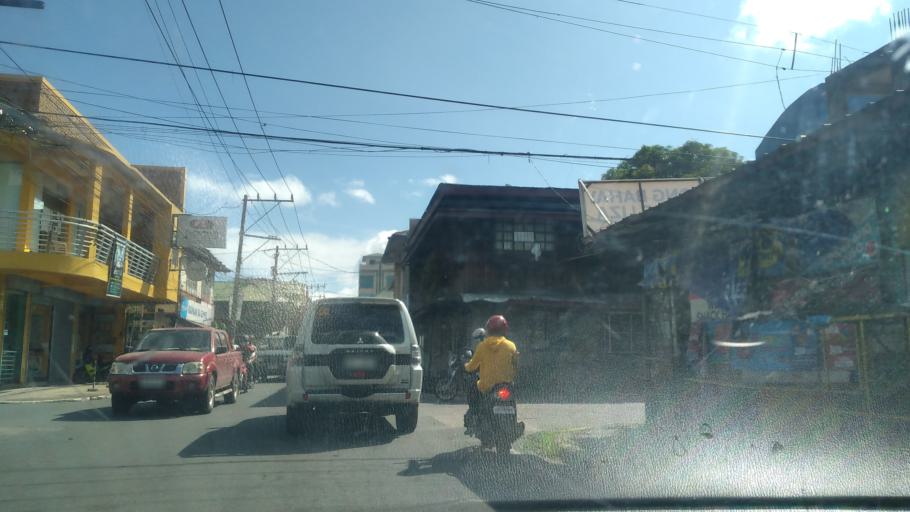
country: PH
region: Calabarzon
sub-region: Province of Quezon
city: Lucena
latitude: 13.9381
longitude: 121.6117
